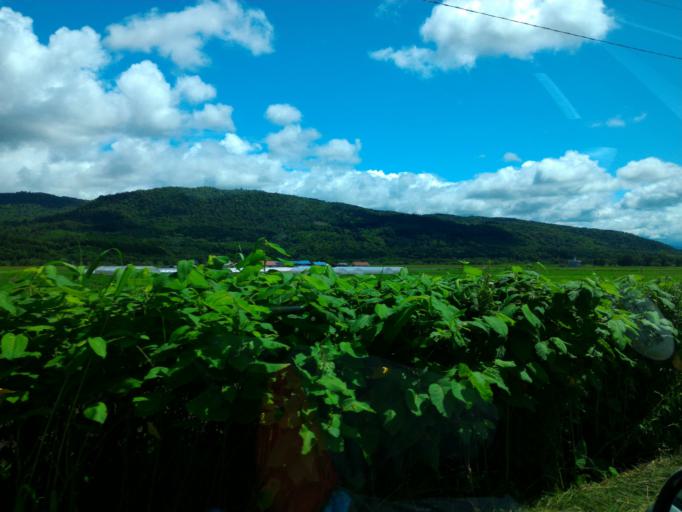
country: JP
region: Hokkaido
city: Nayoro
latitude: 44.5675
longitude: 142.3156
